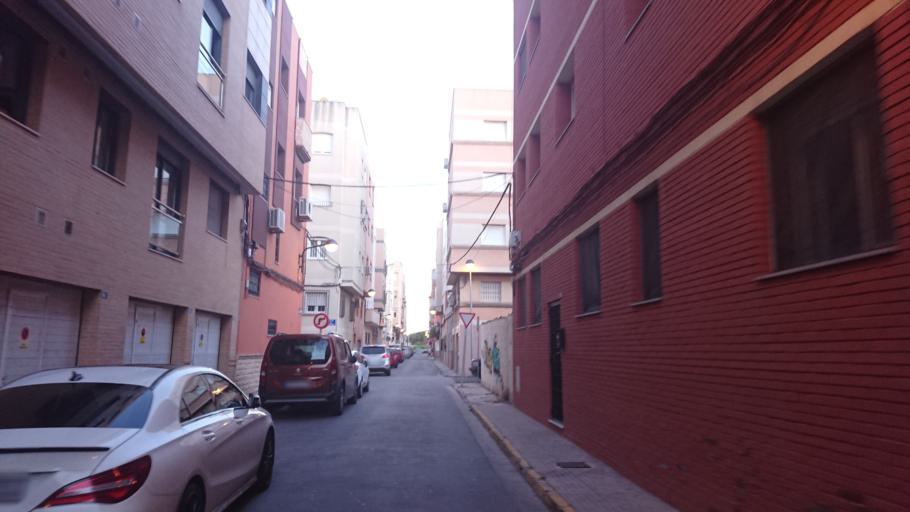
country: ES
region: Melilla
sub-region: Melilla
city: Melilla
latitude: 35.2786
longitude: -2.9376
